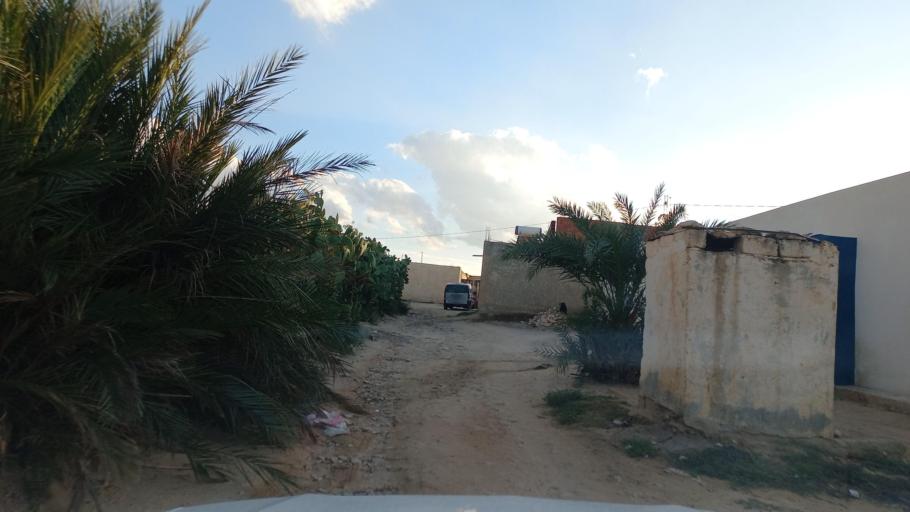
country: TN
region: Al Qasrayn
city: Sbiba
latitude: 35.3805
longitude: 9.0512
